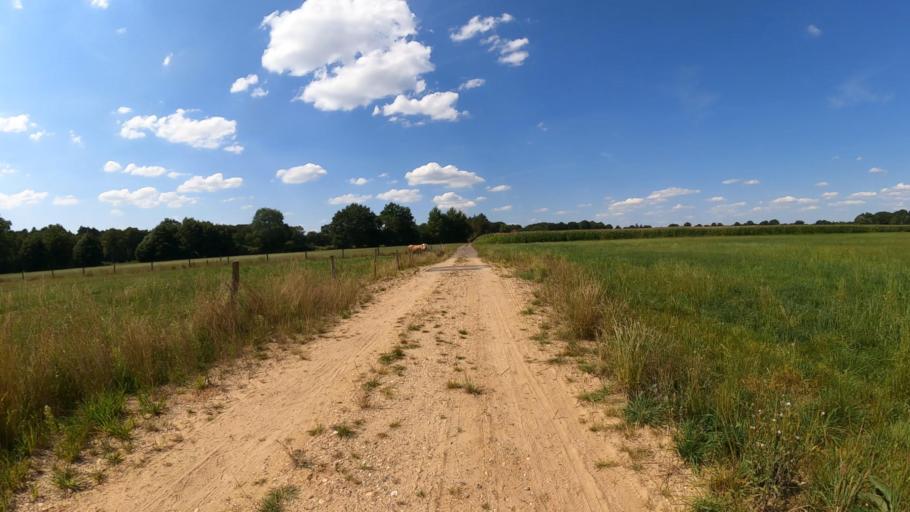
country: DE
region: Schleswig-Holstein
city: Ellerhoop
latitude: 53.7174
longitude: 9.7882
